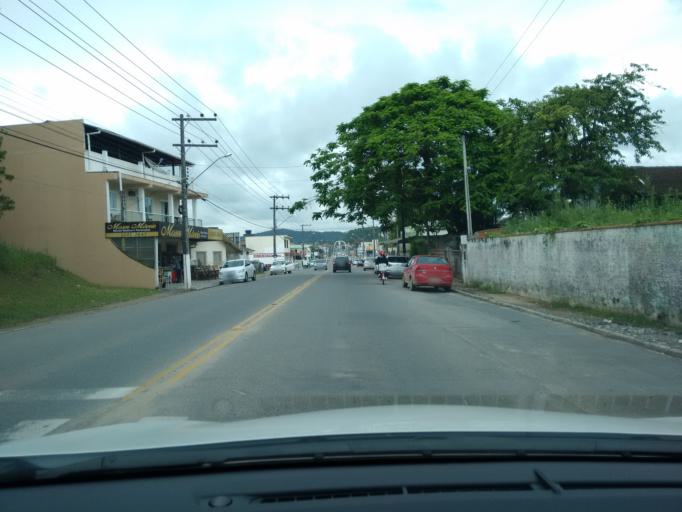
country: BR
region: Santa Catarina
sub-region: Penha
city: Penha
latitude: -26.7595
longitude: -48.6790
